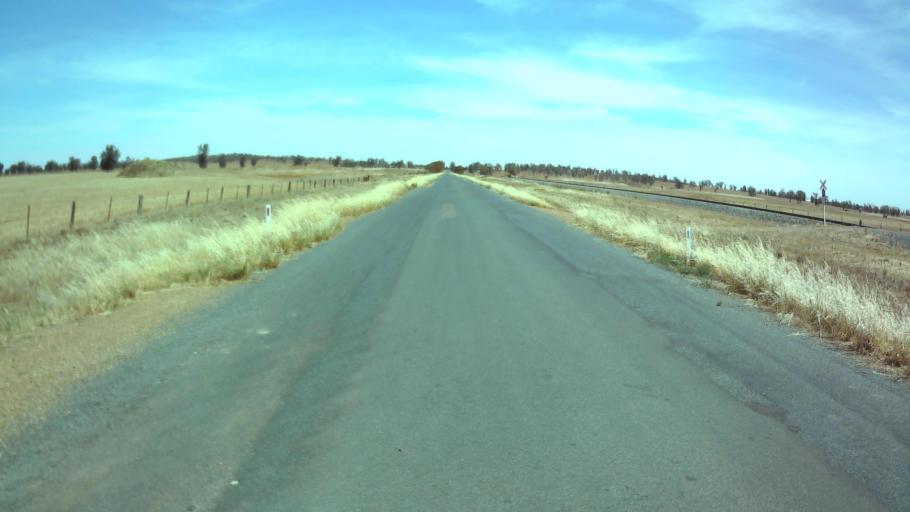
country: AU
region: New South Wales
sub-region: Weddin
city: Grenfell
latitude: -33.7574
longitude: 147.7625
